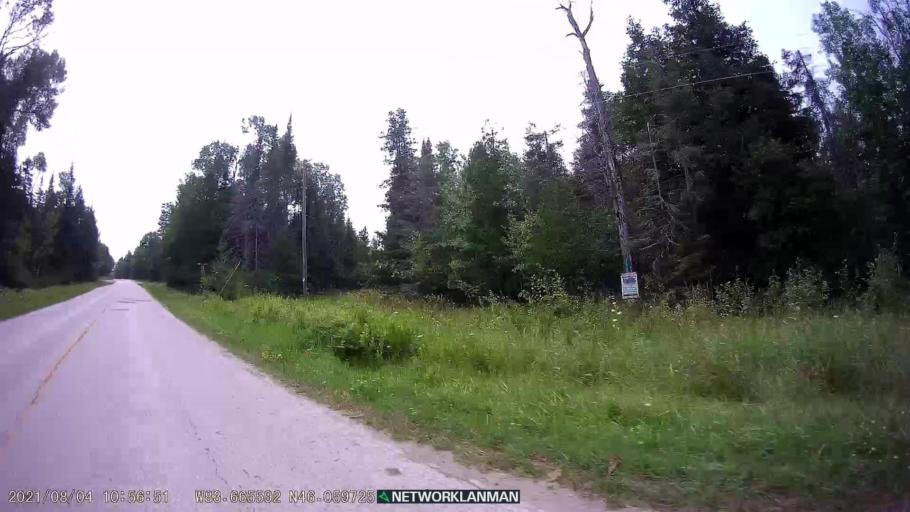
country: CA
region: Ontario
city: Thessalon
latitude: 46.0585
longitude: -83.6657
